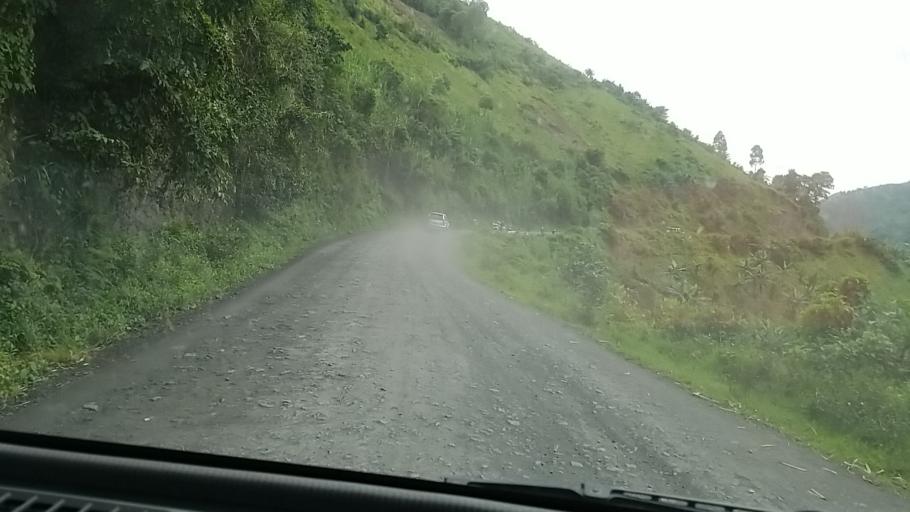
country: CD
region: Nord Kivu
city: Sake
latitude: -1.7427
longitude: 28.9913
